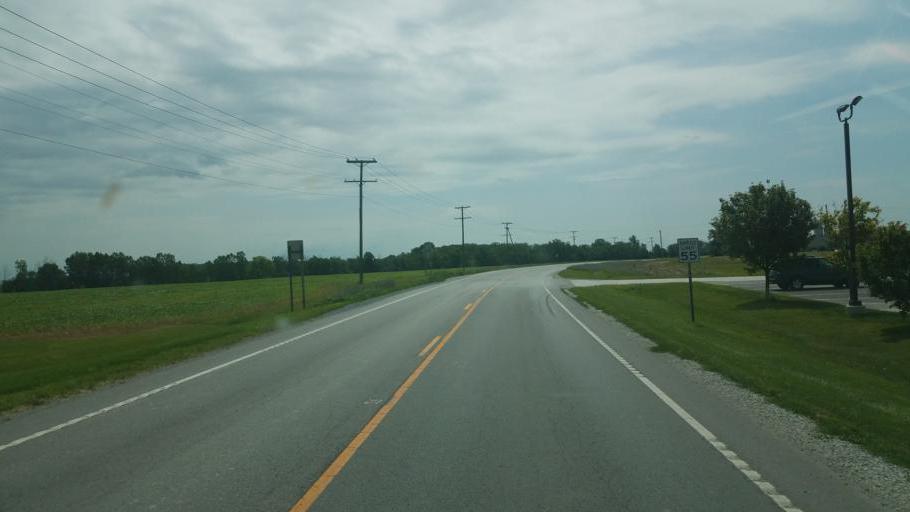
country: US
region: Ohio
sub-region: Wyandot County
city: Upper Sandusky
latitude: 40.8873
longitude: -83.3269
